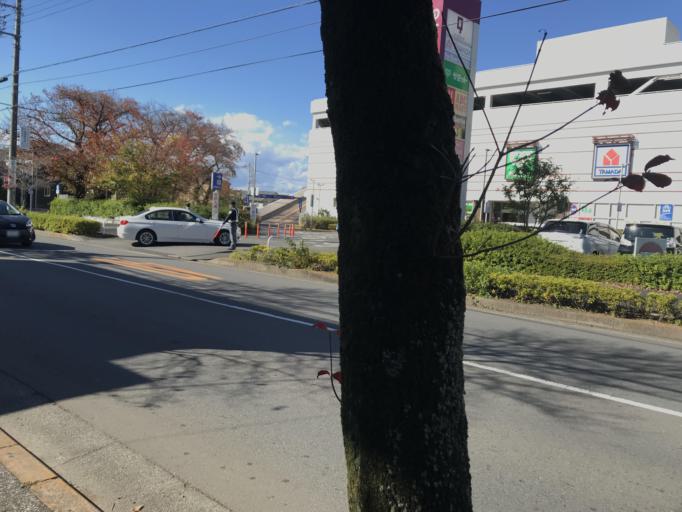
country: JP
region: Tokyo
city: Tanashicho
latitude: 35.7589
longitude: 139.5121
